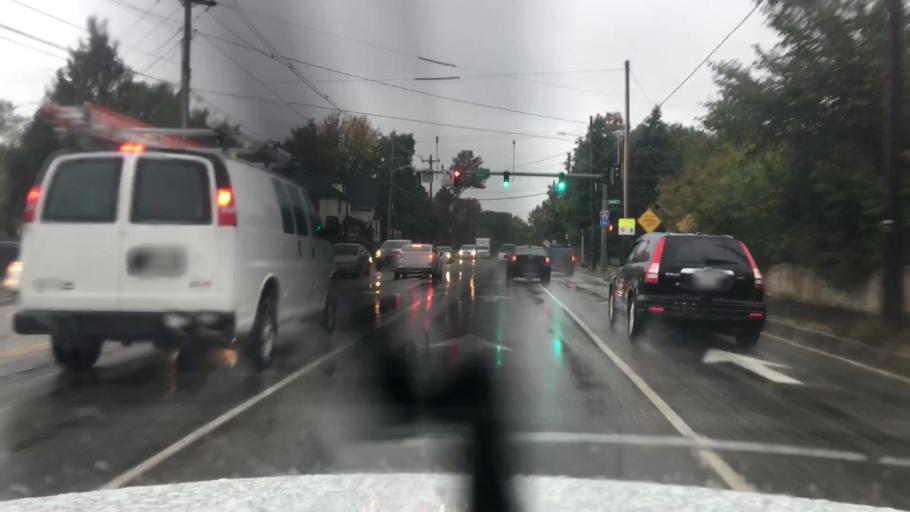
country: US
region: Maine
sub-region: Cumberland County
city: Portland
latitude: 43.6895
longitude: -70.2955
